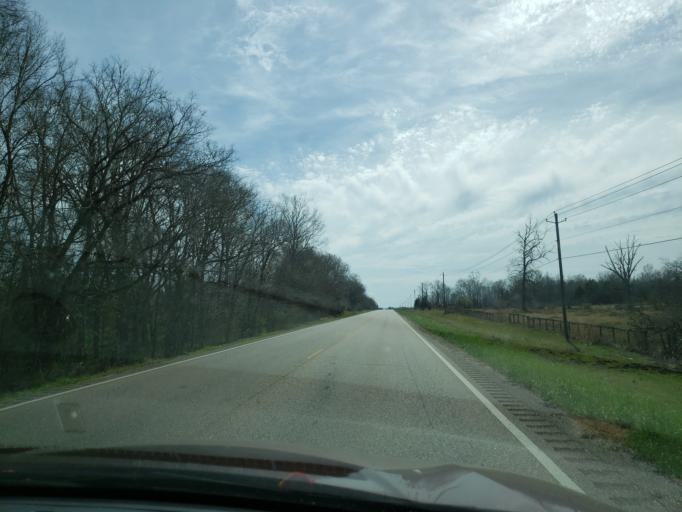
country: US
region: Alabama
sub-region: Dallas County
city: Selma
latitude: 32.4463
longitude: -87.0733
